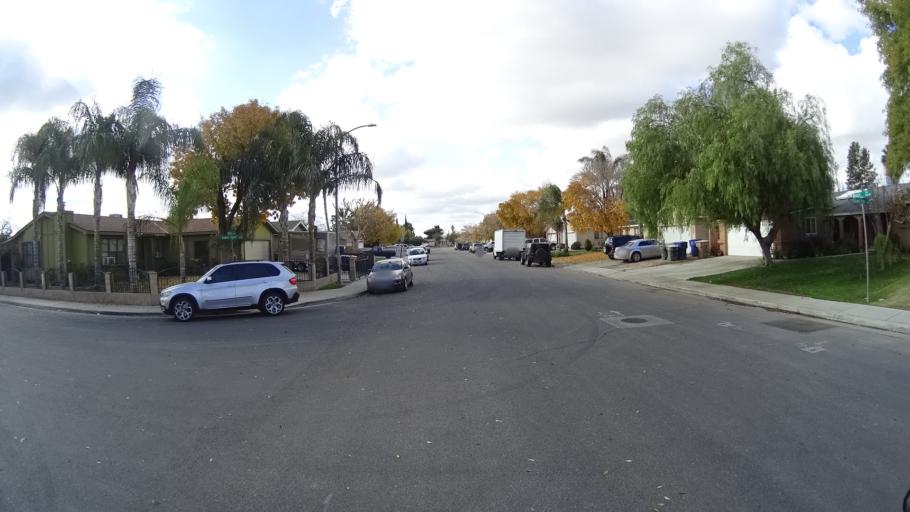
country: US
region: California
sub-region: Kern County
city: Bakersfield
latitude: 35.3585
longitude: -118.9469
